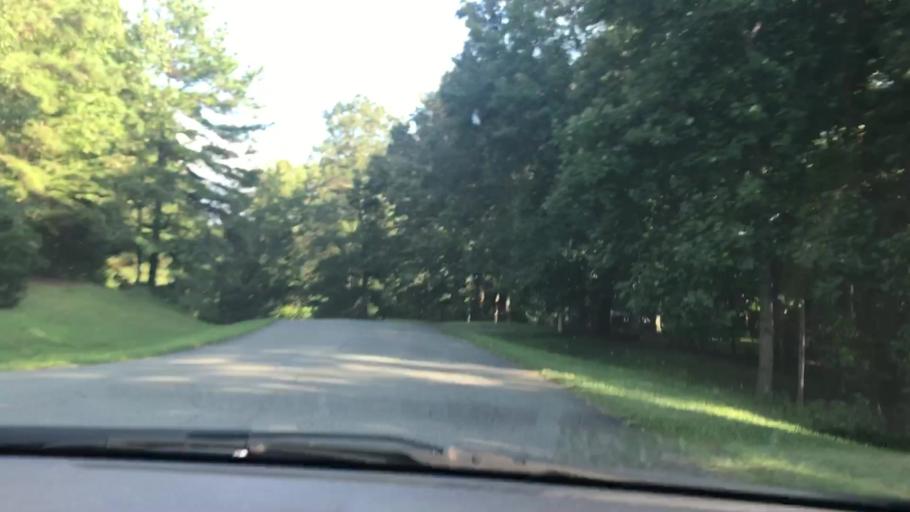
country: US
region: Virginia
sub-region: Henrico County
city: Short Pump
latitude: 37.6098
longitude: -77.7171
